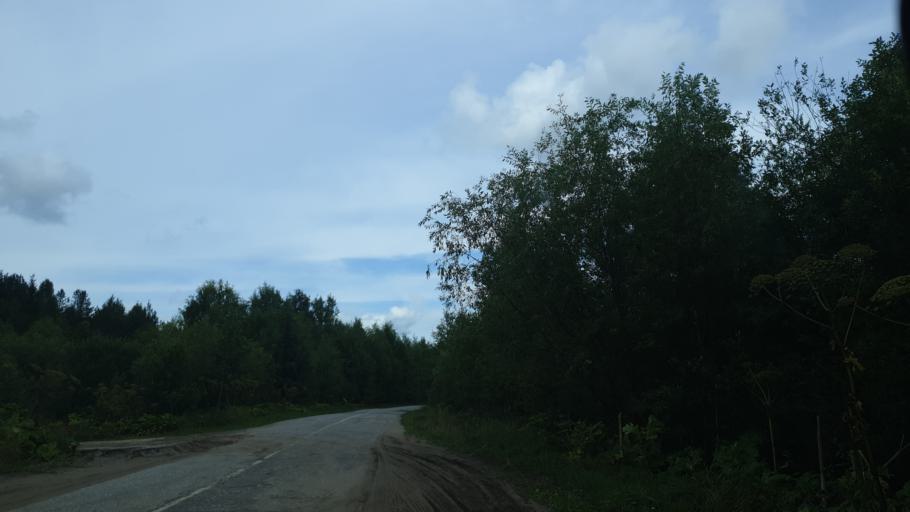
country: RU
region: Komi Republic
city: Aykino
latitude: 62.0902
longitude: 50.1474
